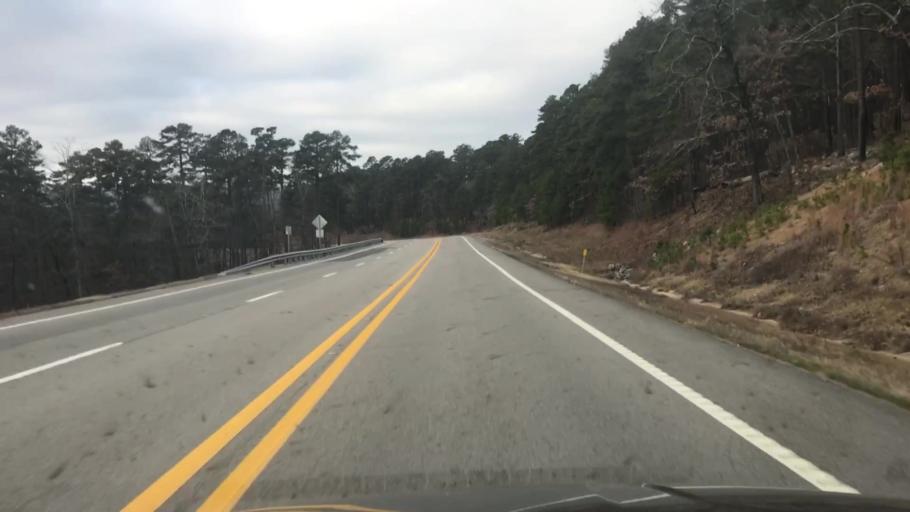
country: US
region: Arkansas
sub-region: Montgomery County
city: Mount Ida
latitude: 34.6833
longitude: -93.7919
